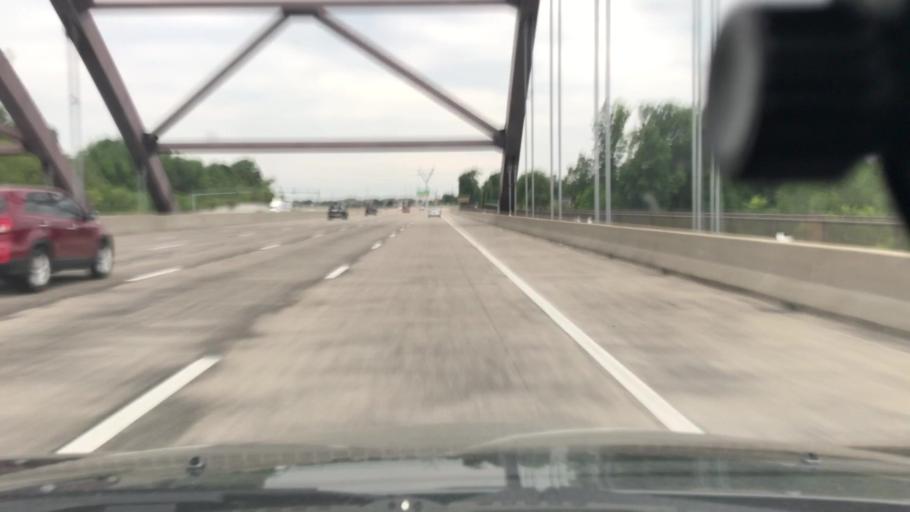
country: US
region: Missouri
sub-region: Saint Charles County
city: Saint Charles
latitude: 38.7376
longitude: -90.5226
